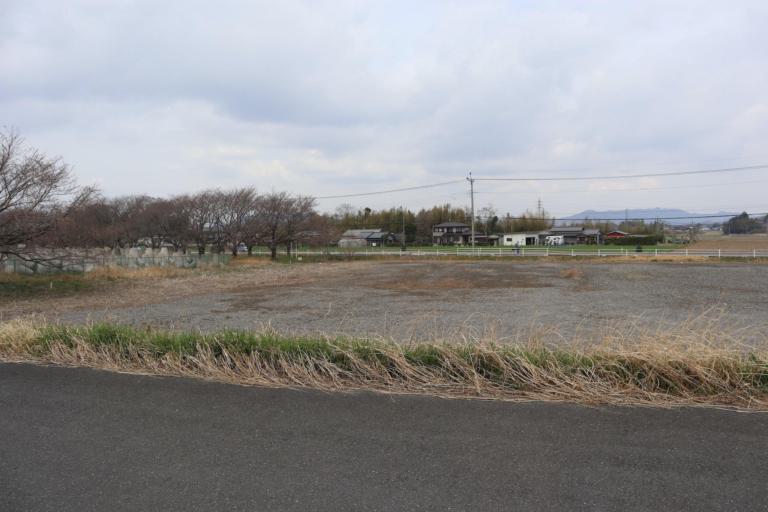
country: JP
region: Tochigi
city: Fujioka
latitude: 36.2659
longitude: 139.6442
